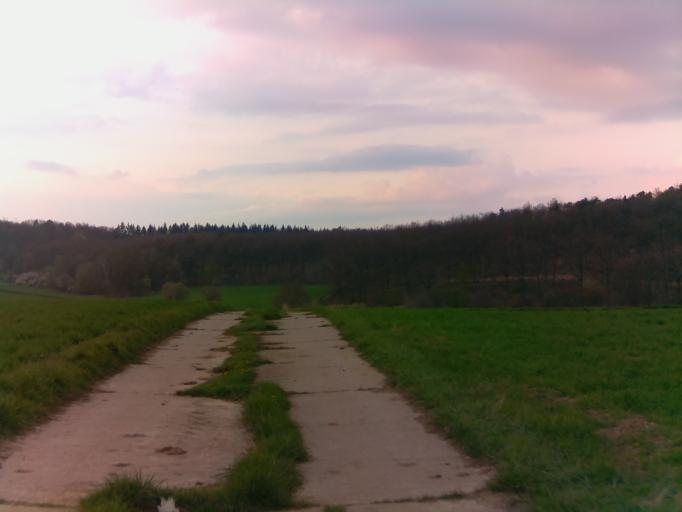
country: DE
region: Rheinland-Pfalz
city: Furfeld
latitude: 49.7817
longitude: 7.8824
